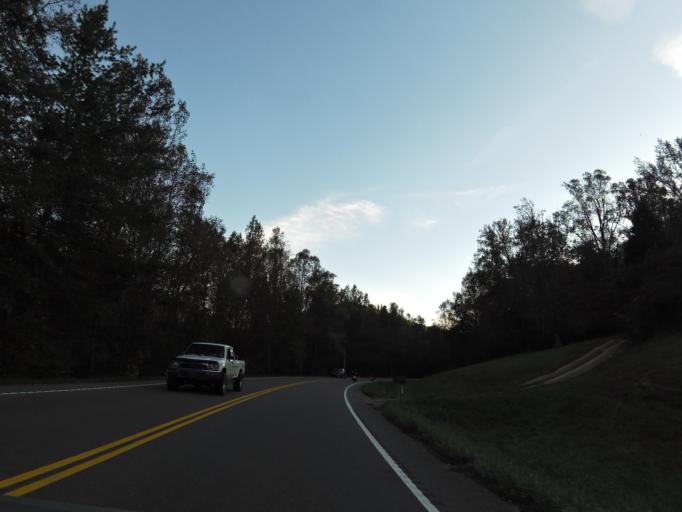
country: US
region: Tennessee
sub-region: Blount County
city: Wildwood
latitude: 35.7098
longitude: -83.8181
